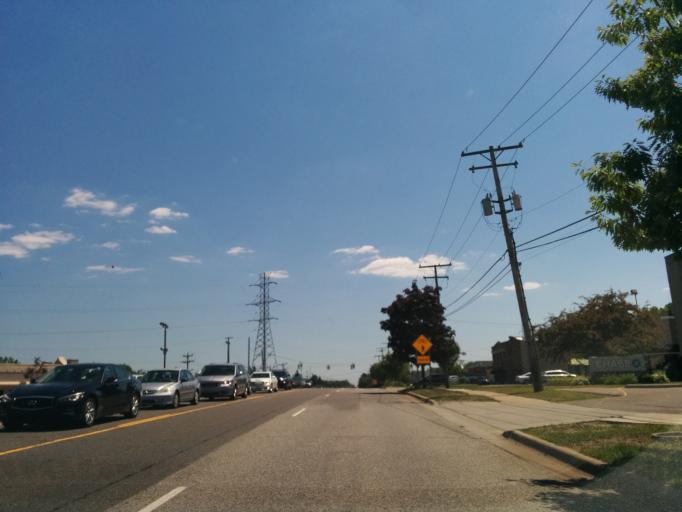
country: US
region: Michigan
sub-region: Oakland County
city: Orchard Lake
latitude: 42.5781
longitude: -83.3625
